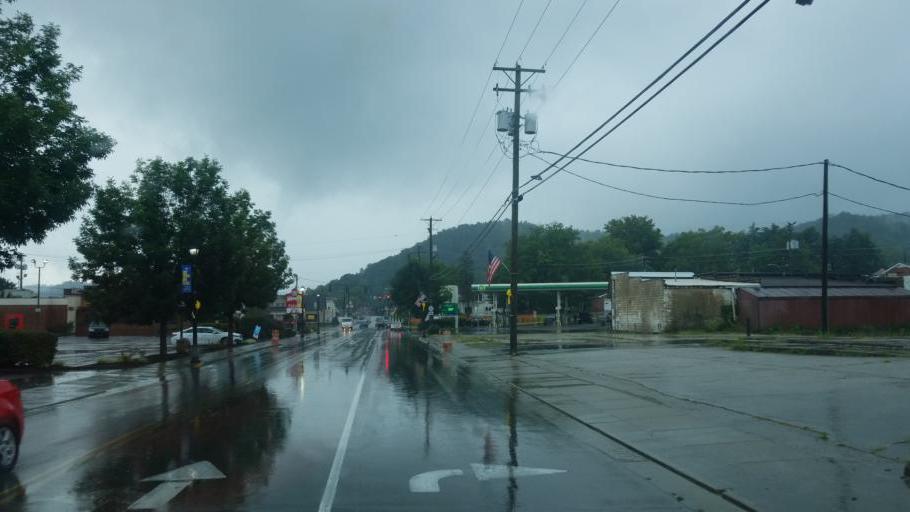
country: US
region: Kentucky
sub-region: Rowan County
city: Morehead
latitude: 38.1788
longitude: -83.4374
